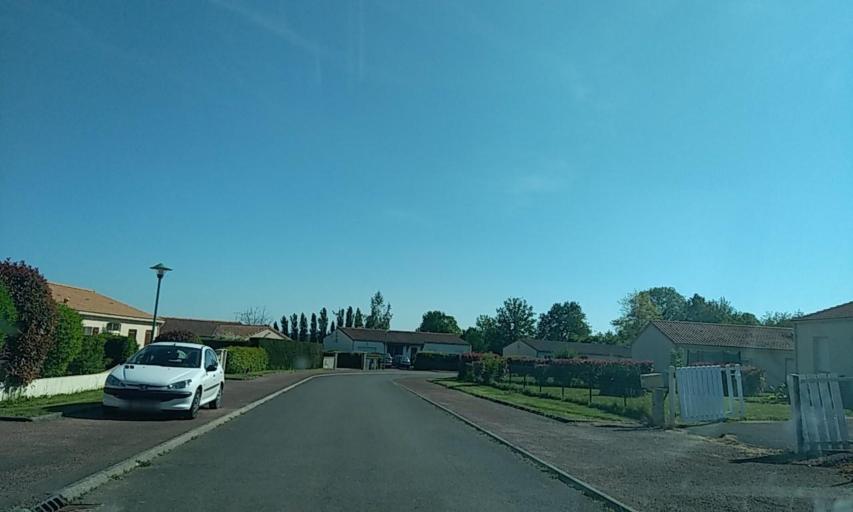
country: FR
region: Poitou-Charentes
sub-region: Departement des Deux-Sevres
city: Boisme
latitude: 46.7790
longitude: -0.4264
